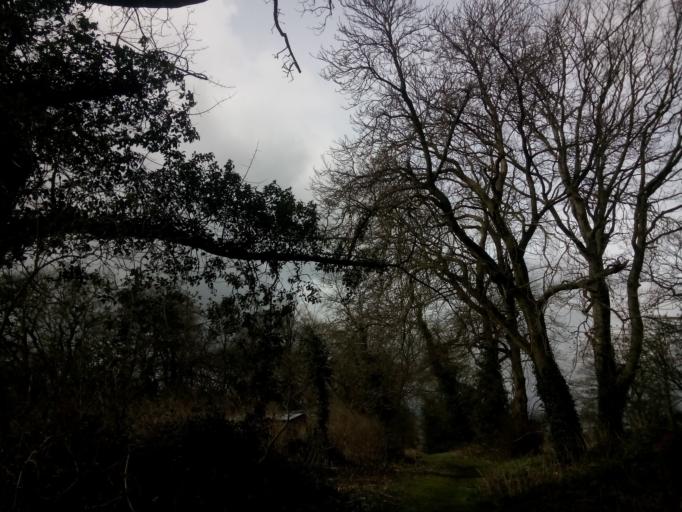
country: GB
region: England
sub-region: County Durham
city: Durham
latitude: 54.7606
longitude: -1.5856
